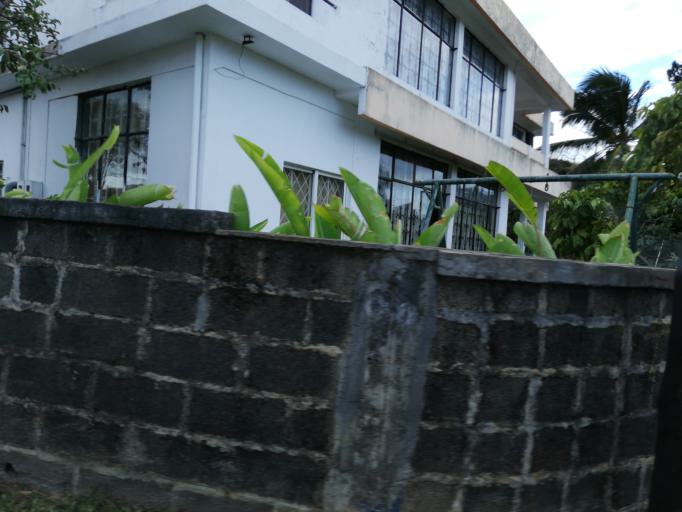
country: MU
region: Plaines Wilhems
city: Quatre Bornes
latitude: -20.2362
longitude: 57.4558
